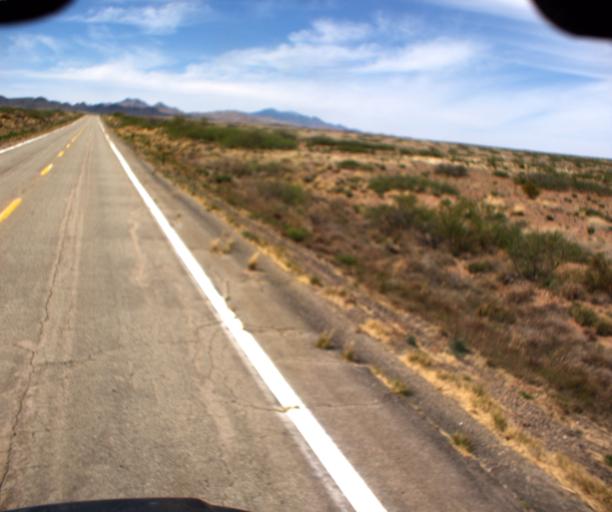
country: US
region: Arizona
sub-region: Cochise County
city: Willcox
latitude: 32.3812
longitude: -109.6500
